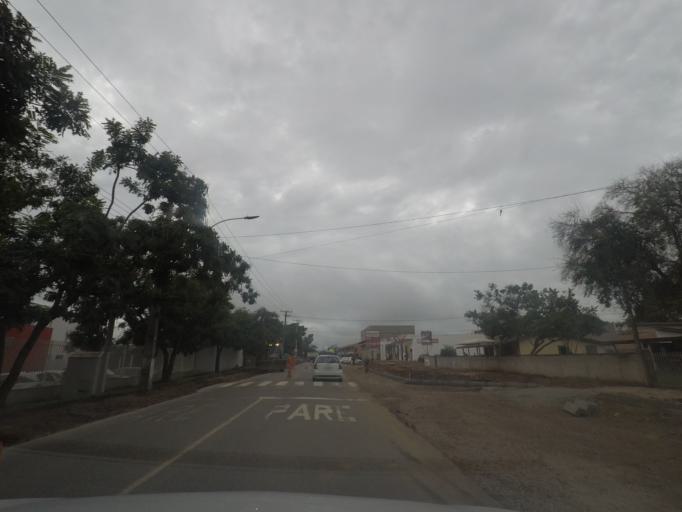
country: BR
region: Parana
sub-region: Piraquara
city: Piraquara
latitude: -25.4525
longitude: -49.0705
